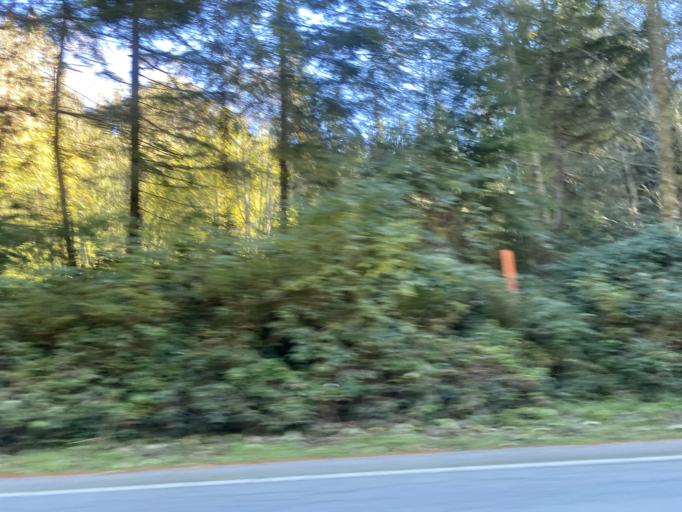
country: US
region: Washington
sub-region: Island County
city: Langley
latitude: 48.0227
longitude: -122.4249
